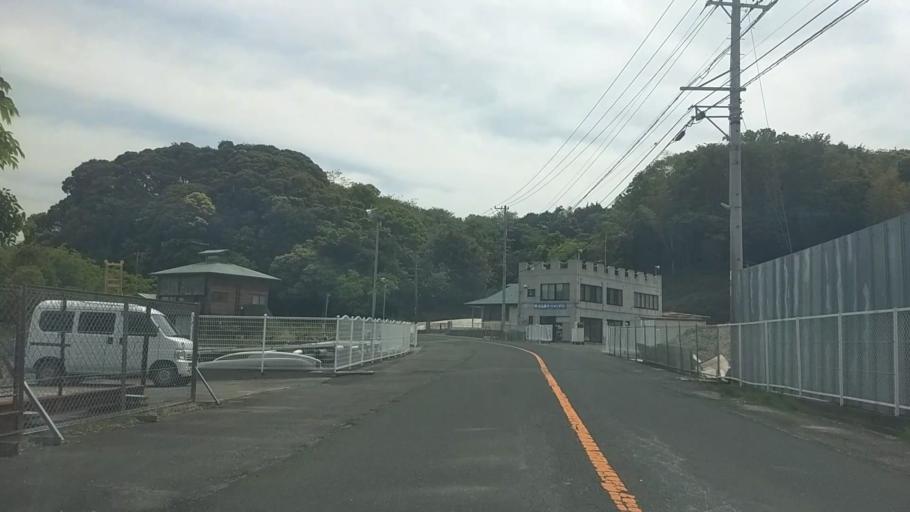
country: JP
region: Shizuoka
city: Kosai-shi
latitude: 34.7538
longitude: 137.5146
